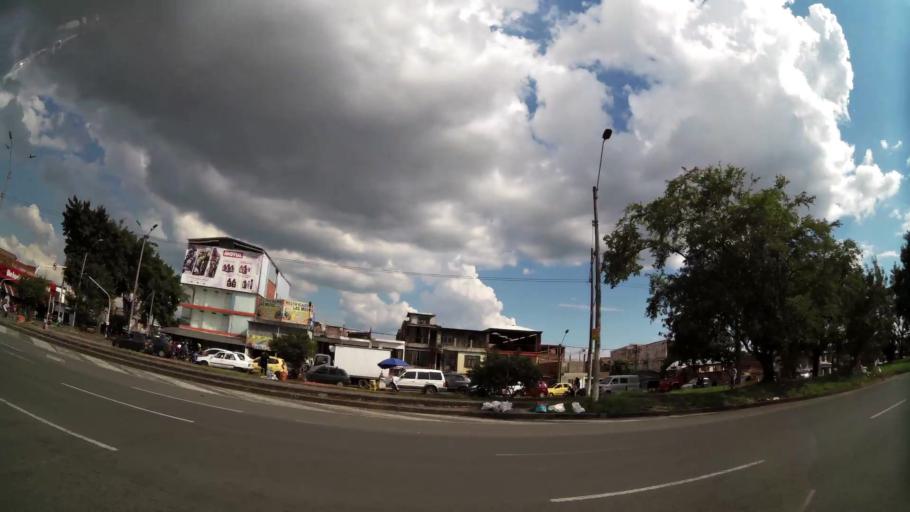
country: CO
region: Valle del Cauca
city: Cali
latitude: 3.4193
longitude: -76.5085
